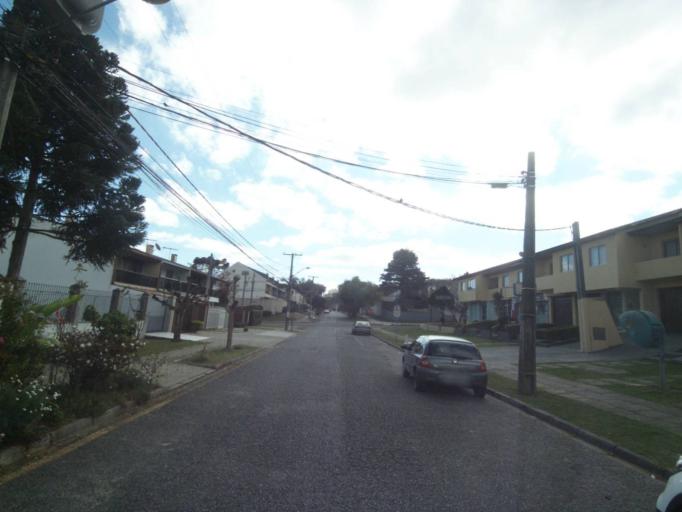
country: BR
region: Parana
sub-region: Curitiba
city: Curitiba
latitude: -25.4608
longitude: -49.2746
